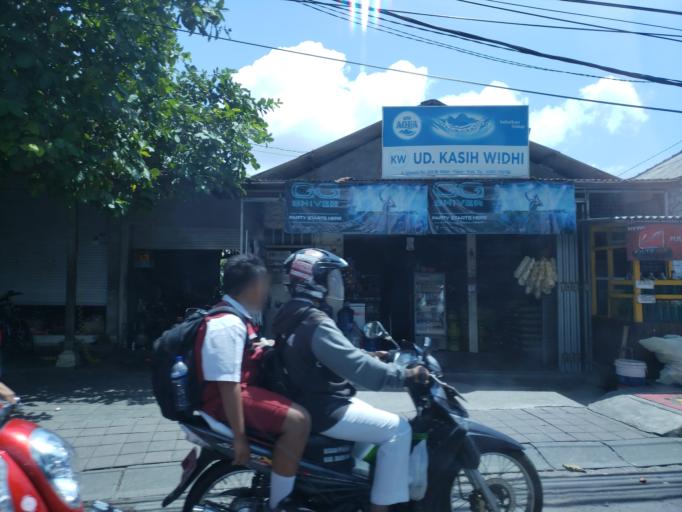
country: ID
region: Bali
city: Kelanabian
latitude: -8.7516
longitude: 115.1787
